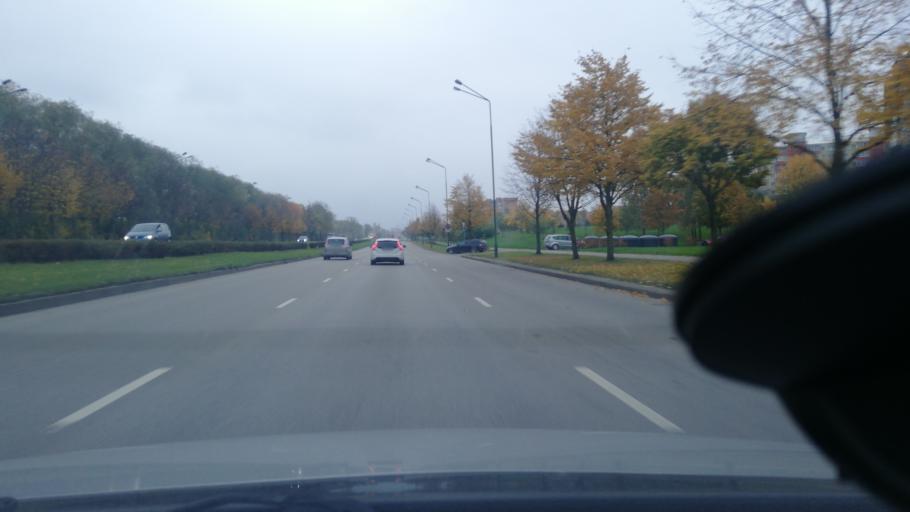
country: LT
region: Klaipedos apskritis
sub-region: Klaipeda
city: Klaipeda
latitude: 55.6745
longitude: 21.1948
